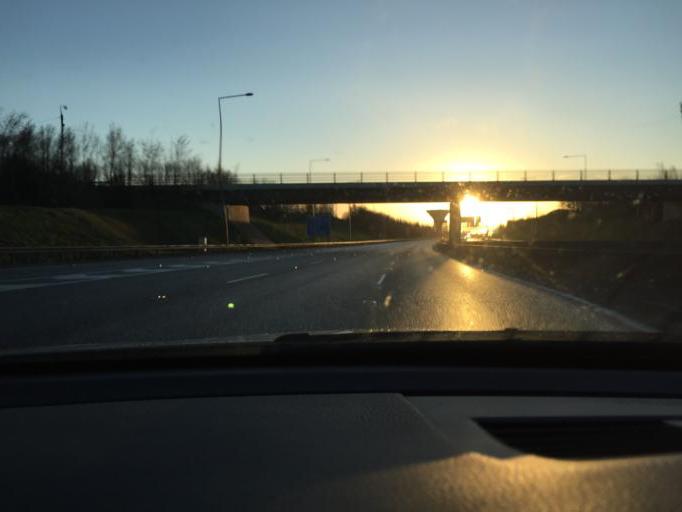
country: IE
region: Leinster
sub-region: Dublin City
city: Finglas
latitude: 53.4069
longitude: -6.3015
